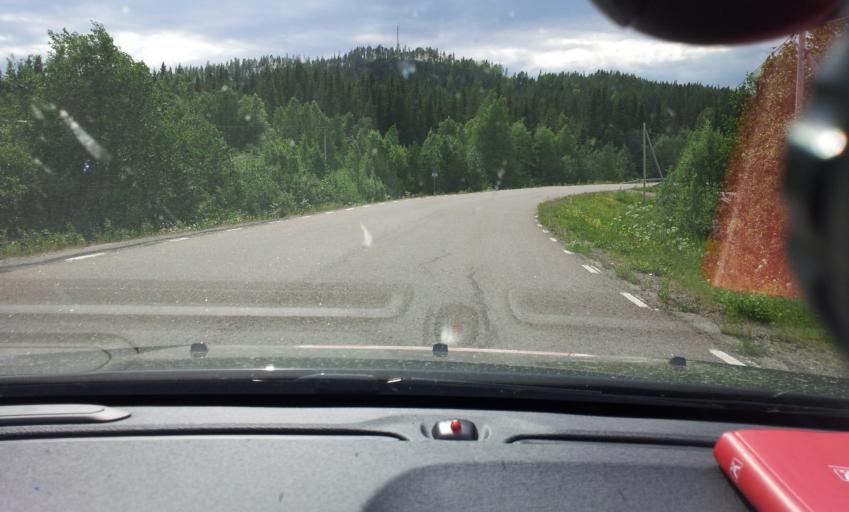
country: SE
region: Jaemtland
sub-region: Bergs Kommun
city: Hoverberg
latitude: 62.6590
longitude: 14.7443
